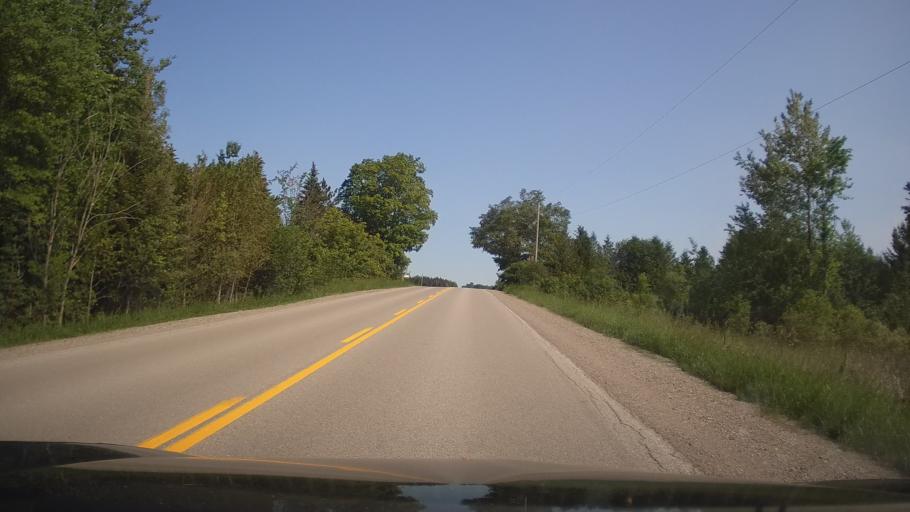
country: CA
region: Ontario
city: Uxbridge
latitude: 44.4760
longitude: -78.9386
